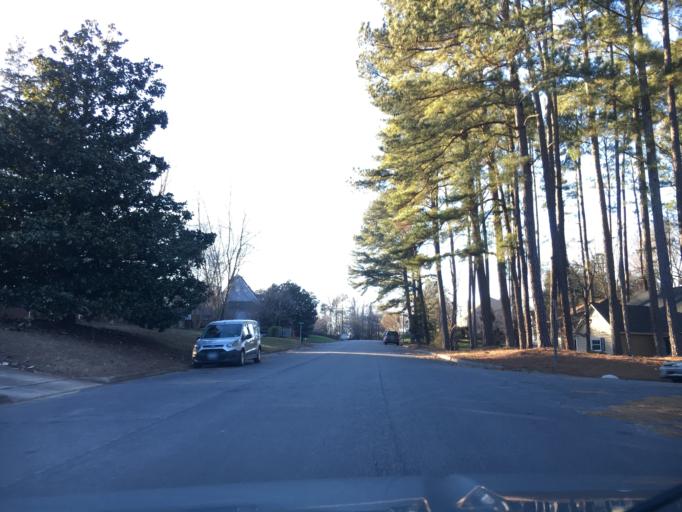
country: US
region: Virginia
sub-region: Halifax County
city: South Boston
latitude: 36.7070
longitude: -78.8836
